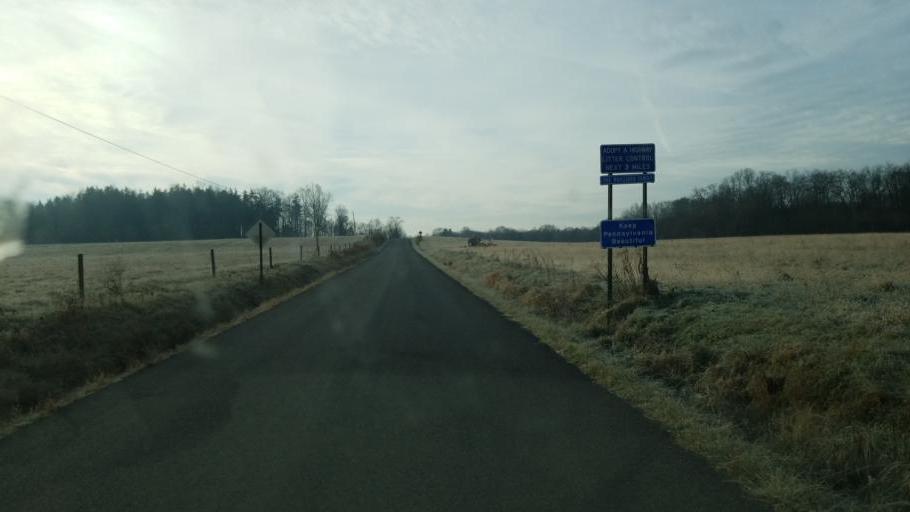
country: US
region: Pennsylvania
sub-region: Crawford County
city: Cochranton
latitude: 41.5252
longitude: -80.1247
